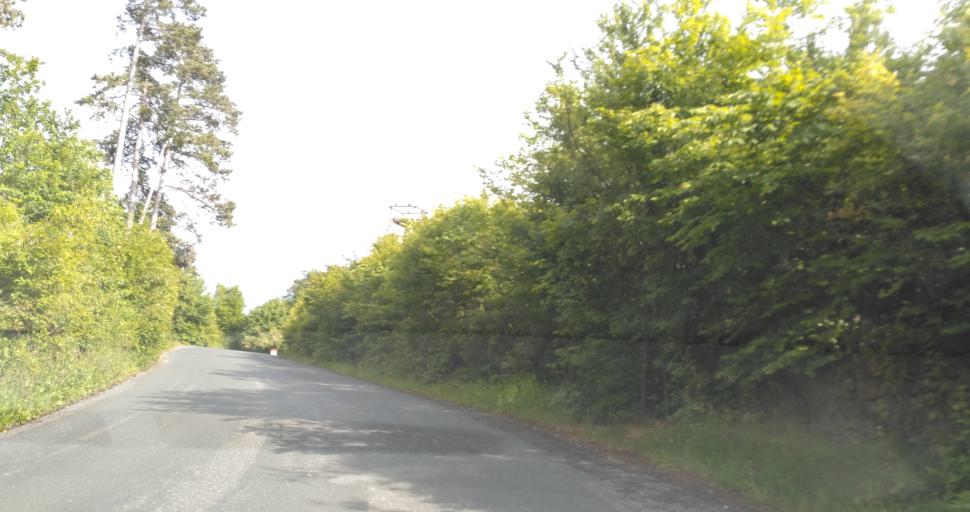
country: CZ
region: Central Bohemia
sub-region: Okres Beroun
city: Beroun
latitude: 49.9107
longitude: 14.0738
